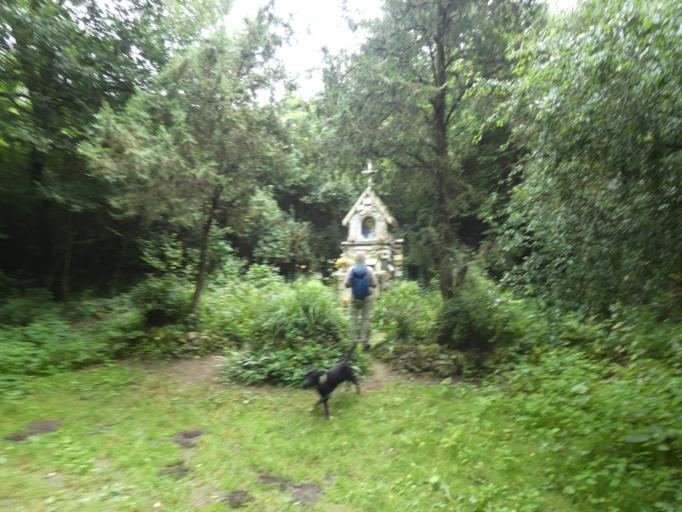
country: HU
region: Pest
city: Szob
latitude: 47.8275
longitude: 18.9012
